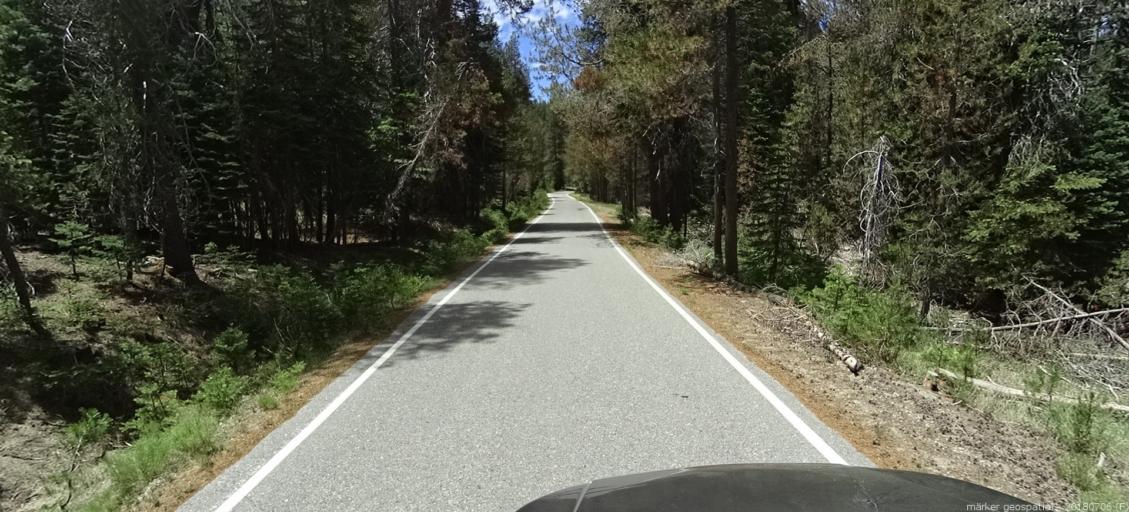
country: US
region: California
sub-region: Madera County
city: Oakhurst
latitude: 37.4446
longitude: -119.4648
